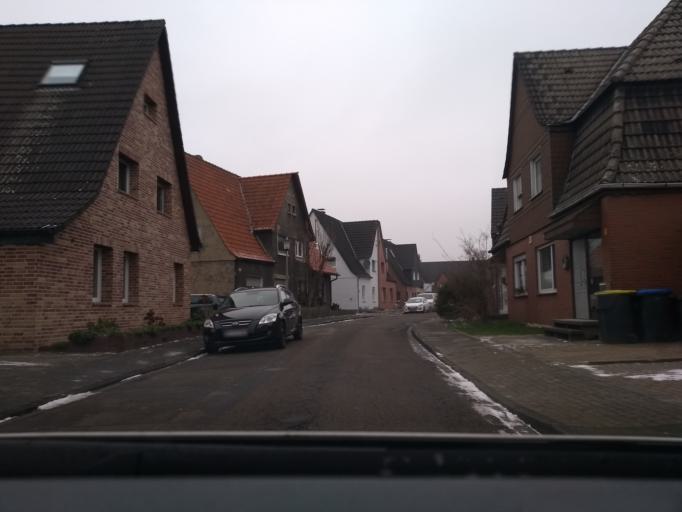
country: DE
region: North Rhine-Westphalia
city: Selm
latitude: 51.6939
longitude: 7.4599
